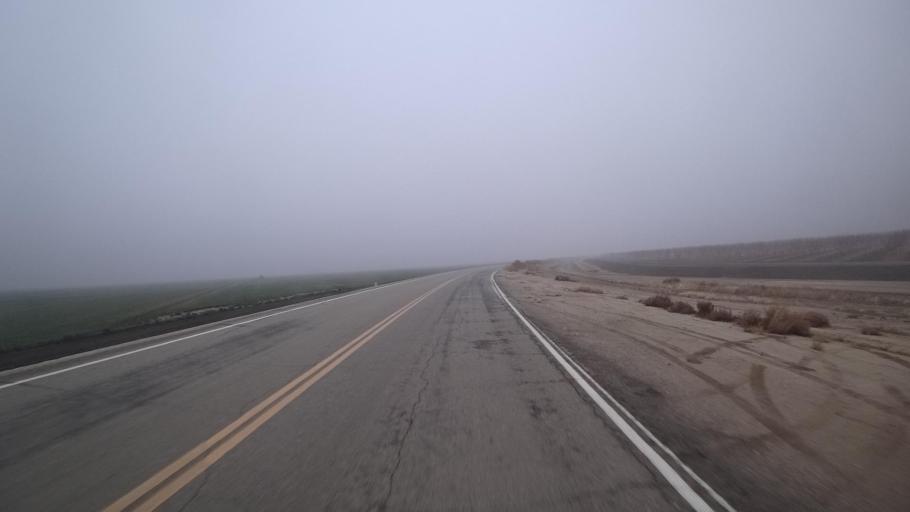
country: US
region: California
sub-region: Kern County
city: Buttonwillow
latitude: 35.4357
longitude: -119.5449
